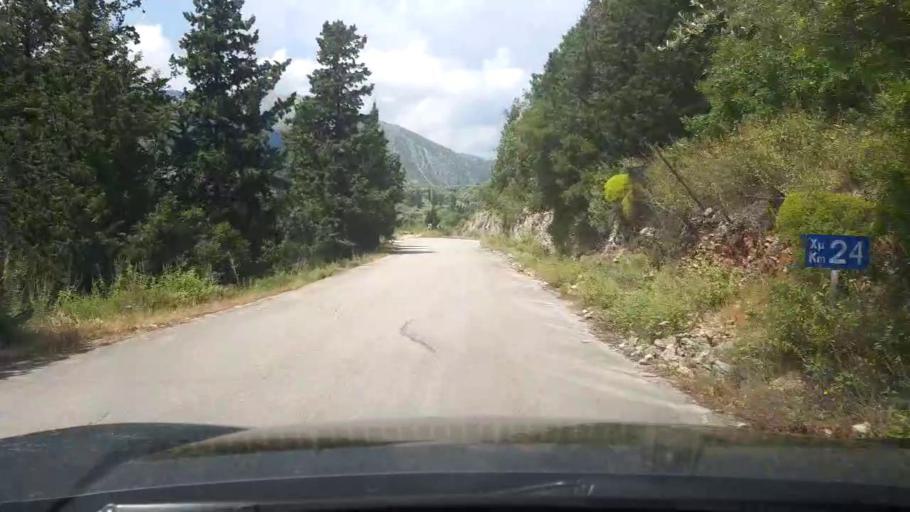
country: GR
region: Ionian Islands
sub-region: Lefkada
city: Nidri
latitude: 38.6481
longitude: 20.7041
